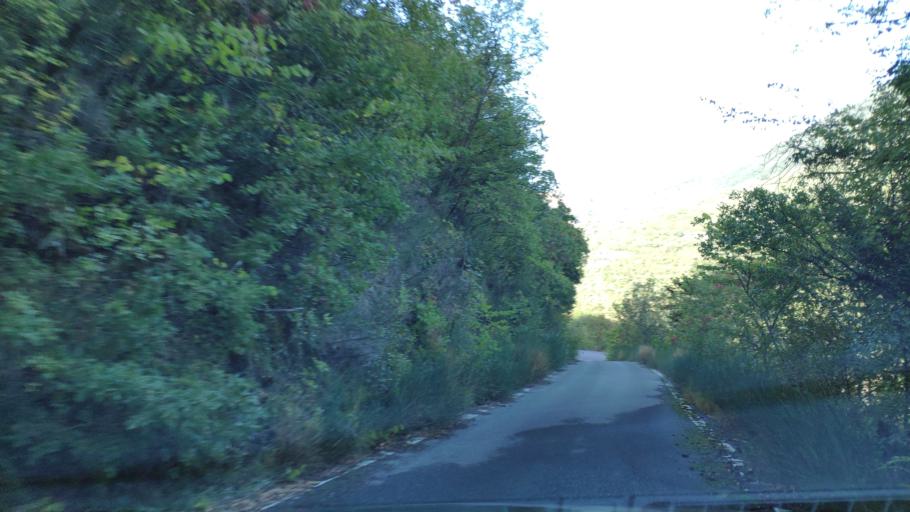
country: GR
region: Peloponnese
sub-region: Nomos Arkadias
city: Dimitsana
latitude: 37.5586
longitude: 22.0428
